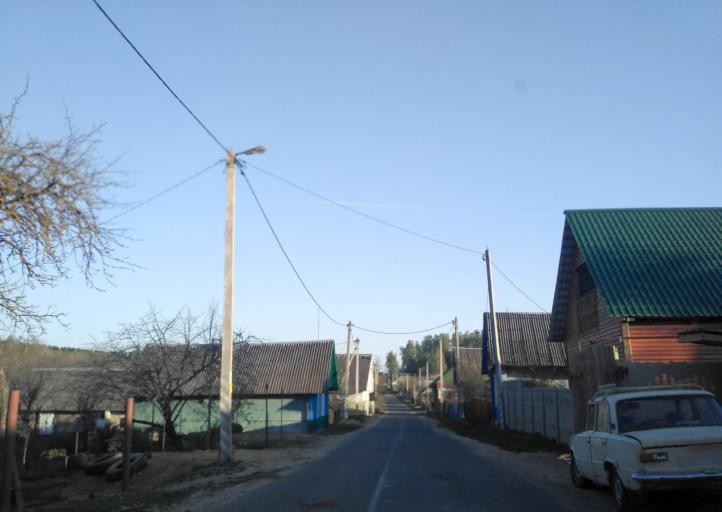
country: BY
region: Minsk
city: Pyatryshki
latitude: 54.1033
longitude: 27.1929
